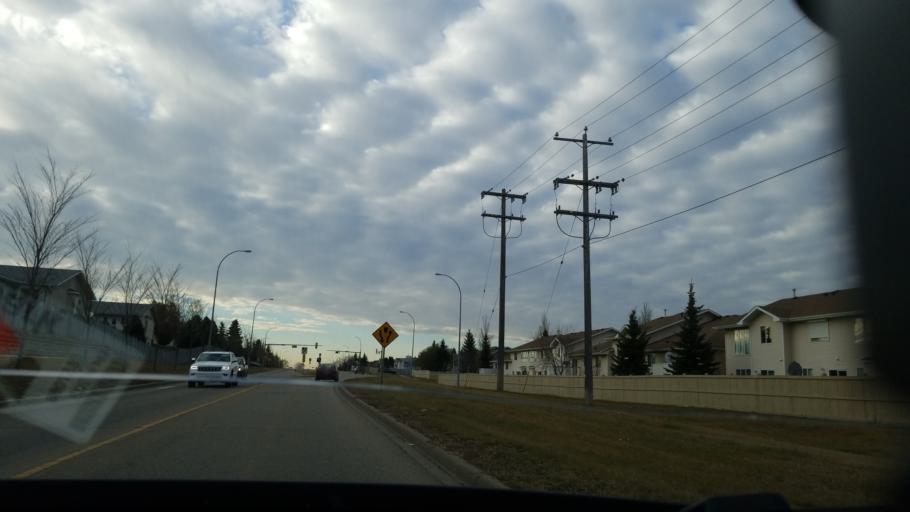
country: CA
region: Alberta
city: Edmonton
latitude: 53.6214
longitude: -113.4428
